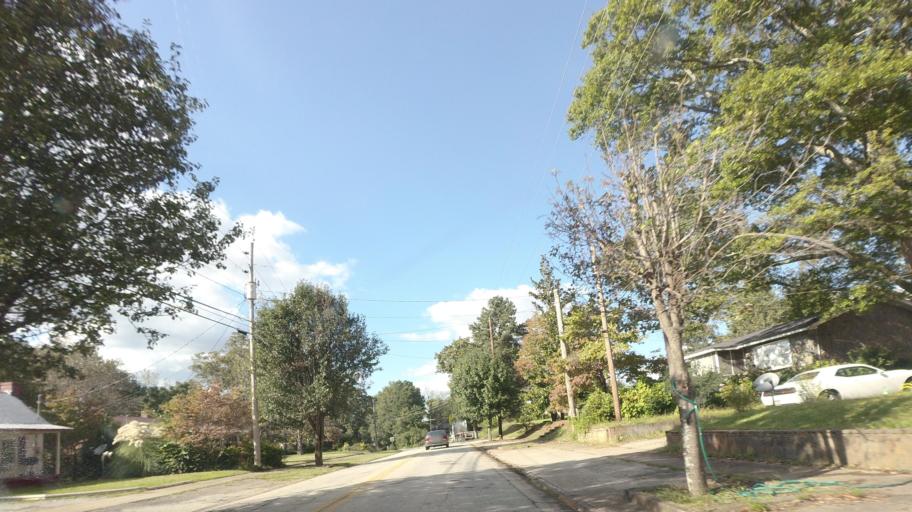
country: US
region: Georgia
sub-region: Lamar County
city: Barnesville
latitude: 33.0641
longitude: -84.1555
